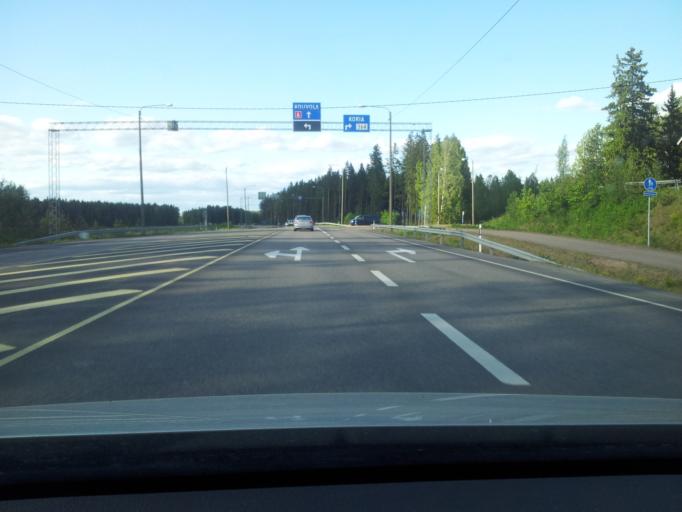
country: FI
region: Kymenlaakso
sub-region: Kouvola
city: Elimaeki
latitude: 60.8258
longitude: 26.5362
